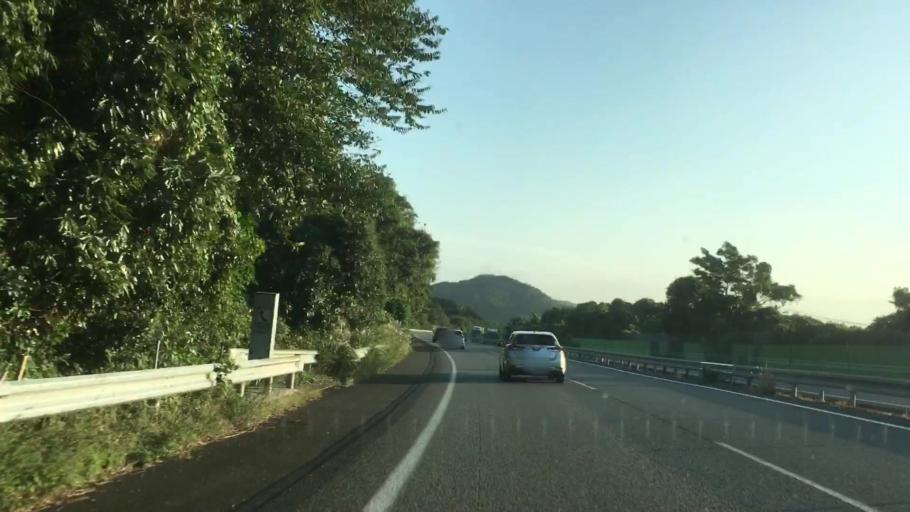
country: JP
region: Yamaguchi
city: Shimonoseki
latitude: 34.0190
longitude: 130.9580
